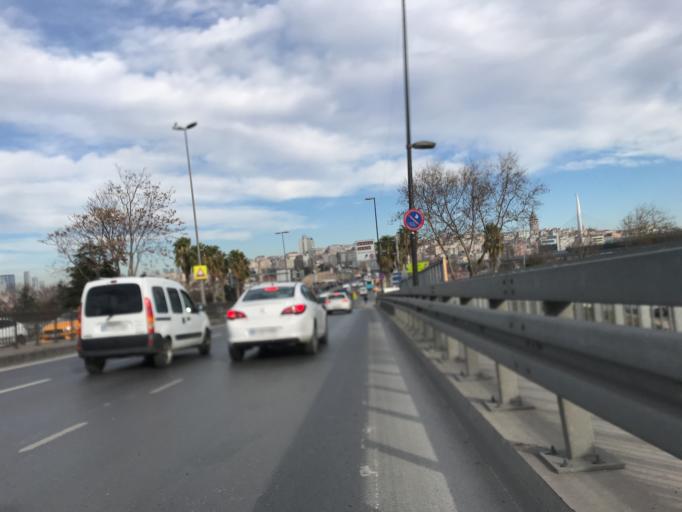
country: TR
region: Istanbul
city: Eminoenue
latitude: 41.0223
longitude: 28.9612
